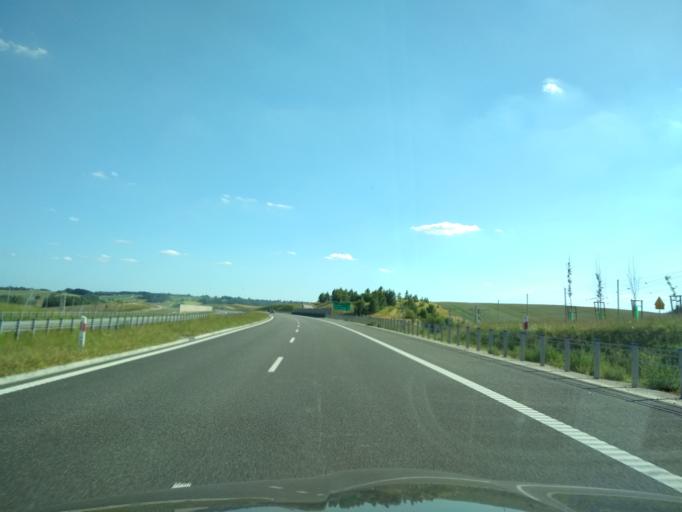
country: PL
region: Subcarpathian Voivodeship
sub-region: Rzeszow
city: Przybyszowka
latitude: 50.0604
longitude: 21.9242
